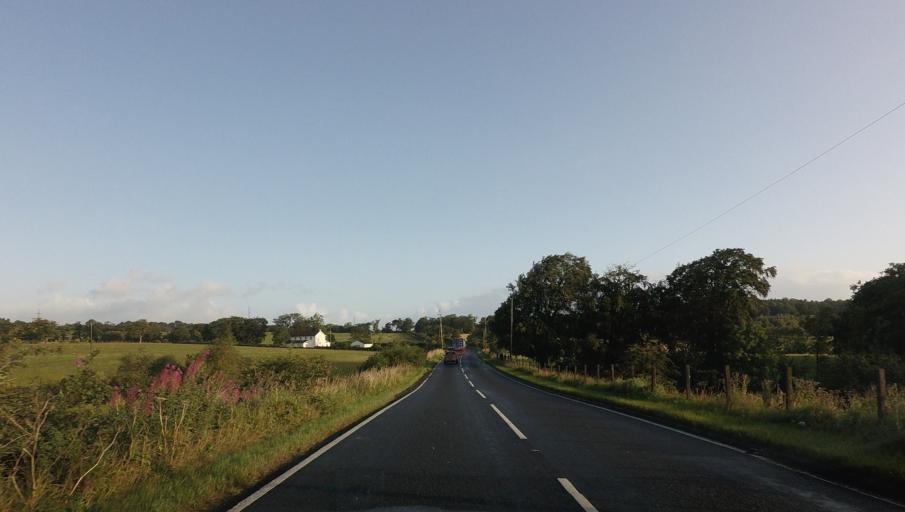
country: GB
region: Scotland
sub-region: Falkirk
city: Polmont
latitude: 55.9494
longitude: -3.6821
